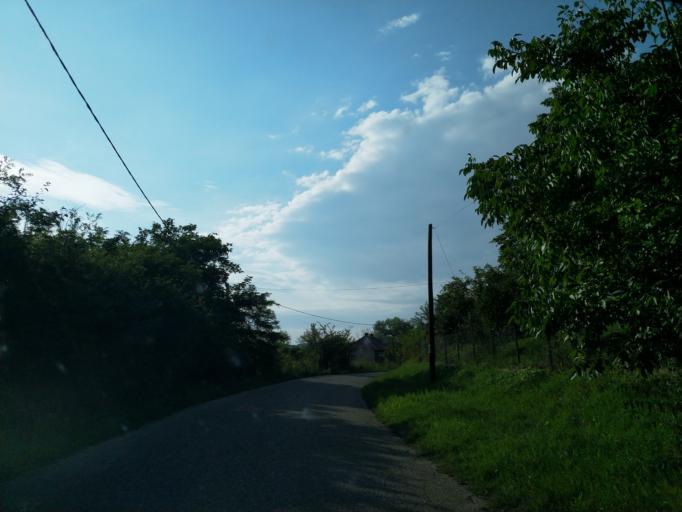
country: RS
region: Central Serbia
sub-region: Pomoravski Okrug
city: Jagodina
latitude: 44.0028
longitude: 21.1844
